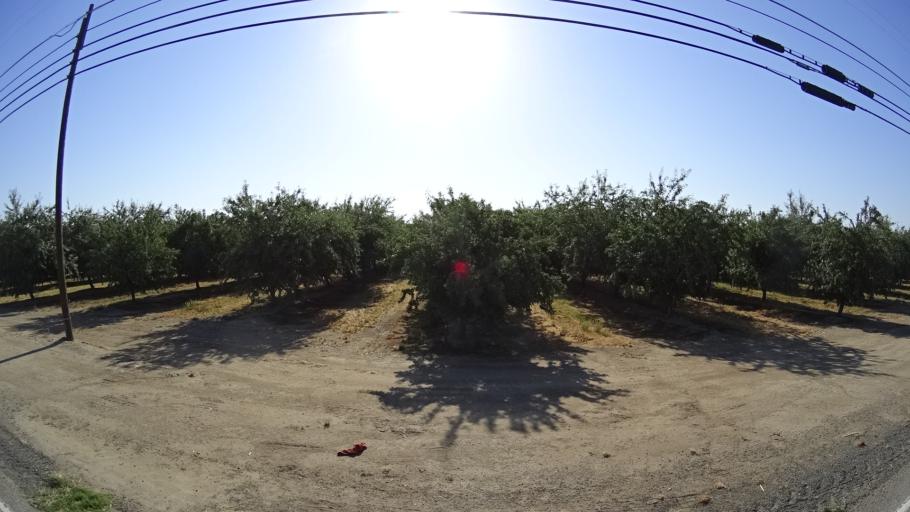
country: US
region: California
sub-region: Kings County
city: Lucerne
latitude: 36.3638
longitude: -119.7090
